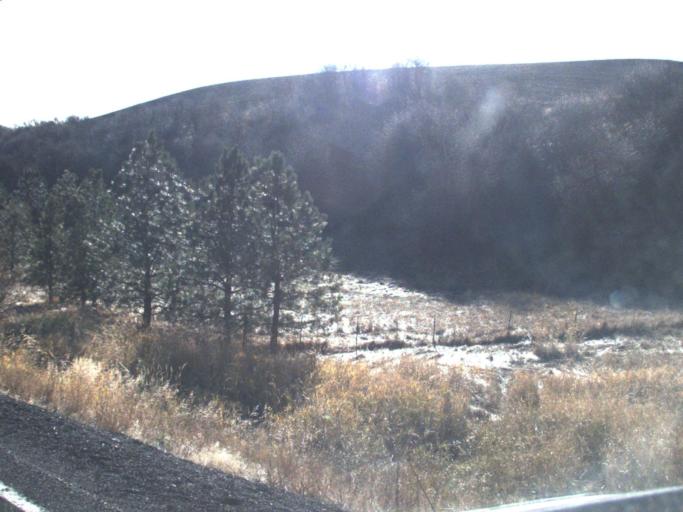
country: US
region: Washington
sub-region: Whitman County
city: Pullman
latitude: 46.7261
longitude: -117.2920
